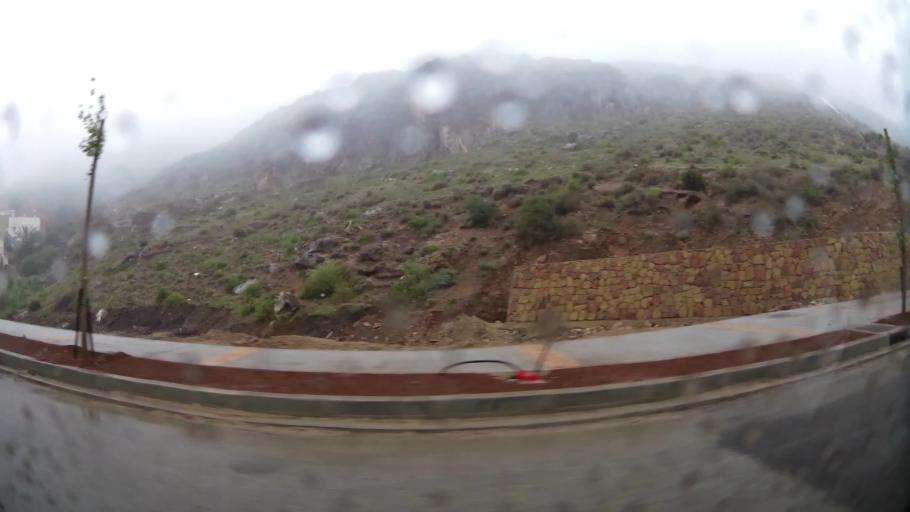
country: MA
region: Taza-Al Hoceima-Taounate
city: Tirhanimine
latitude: 35.2345
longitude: -3.9504
